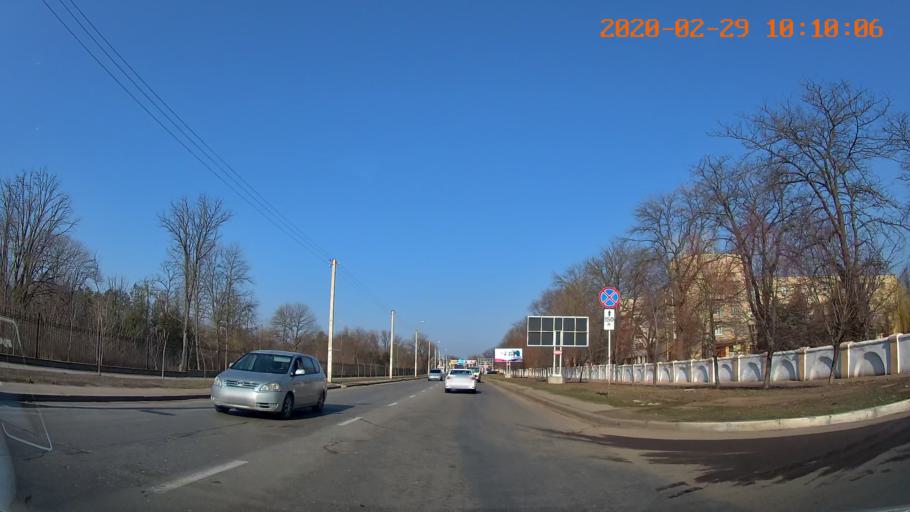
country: MD
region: Telenesti
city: Tiraspolul Nou
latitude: 46.8314
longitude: 29.6468
